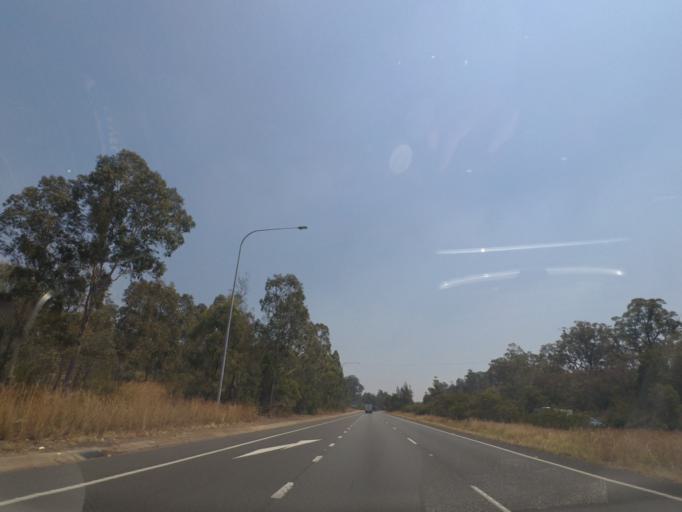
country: AU
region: New South Wales
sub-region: Newcastle
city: Beresfield
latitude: -32.8321
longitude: 151.6343
